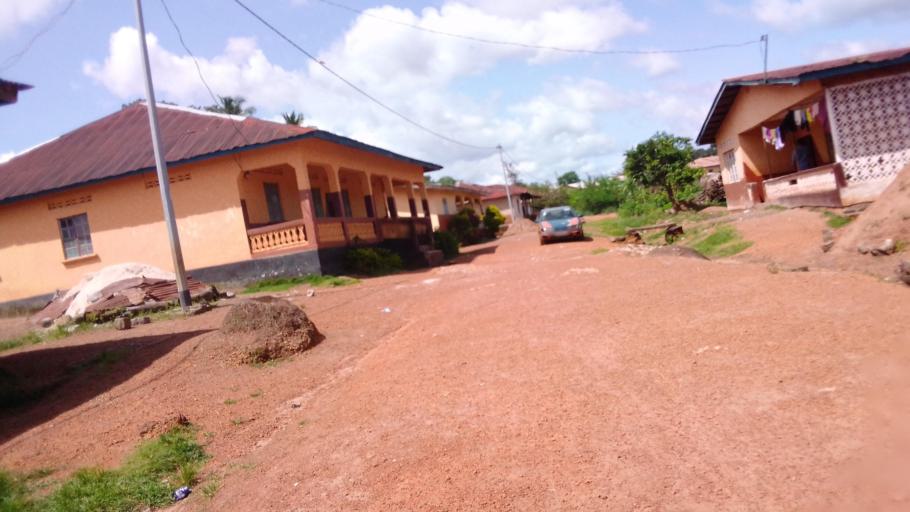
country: SL
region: Northern Province
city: Makeni
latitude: 8.8820
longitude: -12.0414
